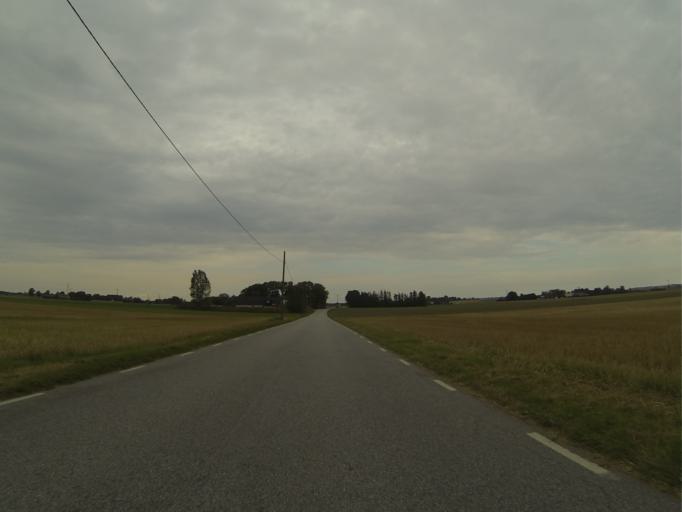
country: SE
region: Skane
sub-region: Staffanstorps Kommun
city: Hjaerup
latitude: 55.6498
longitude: 13.1562
